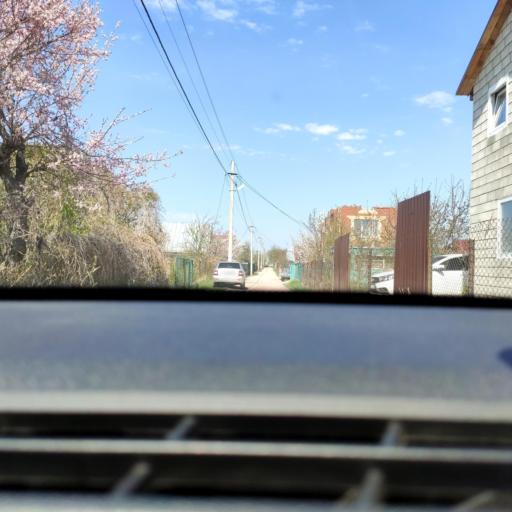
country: RU
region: Samara
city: Tol'yatti
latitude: 53.5932
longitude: 49.3007
